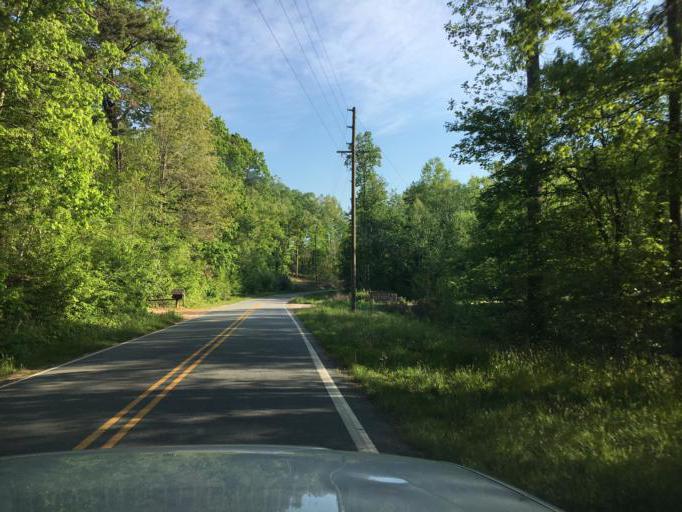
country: US
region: North Carolina
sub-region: Rutherford County
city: Rutherfordton
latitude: 35.3010
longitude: -82.0059
